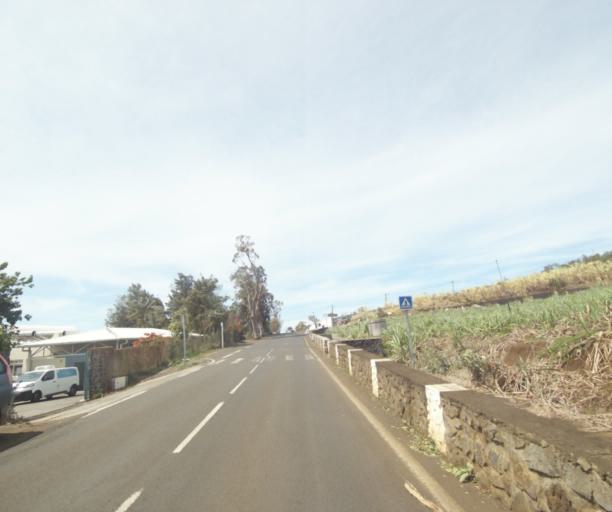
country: RE
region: Reunion
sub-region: Reunion
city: Saint-Paul
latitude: -21.0387
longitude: 55.2882
